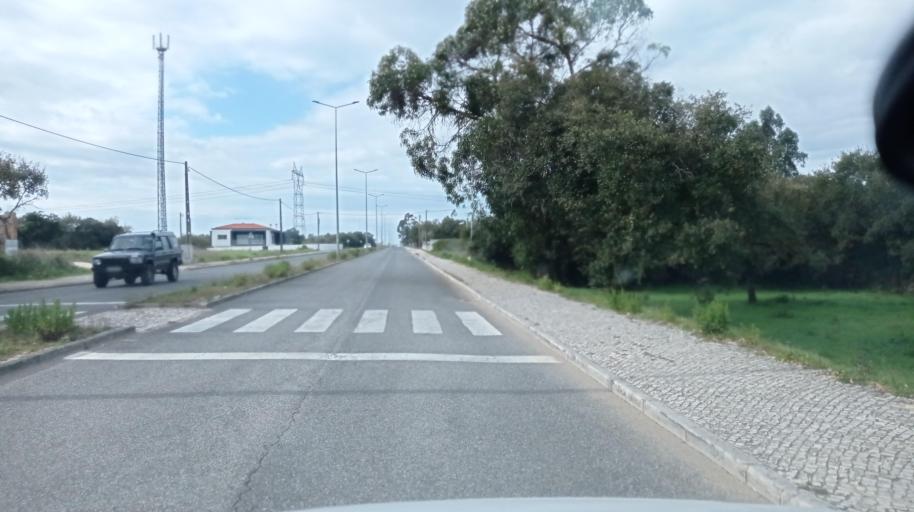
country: PT
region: Leiria
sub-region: Alcobaca
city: Benedita
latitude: 39.4243
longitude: -8.9631
